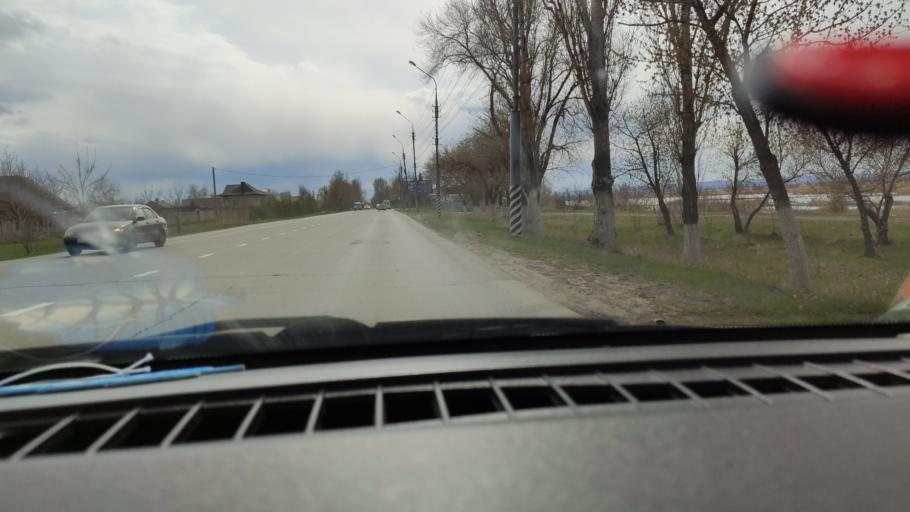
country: RU
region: Saratov
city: Privolzhskiy
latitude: 51.4339
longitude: 46.0583
